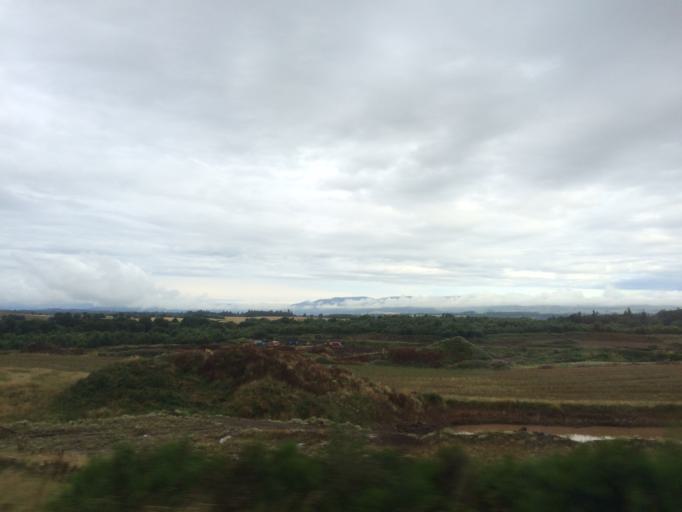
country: GB
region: Scotland
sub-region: Perth and Kinross
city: Auchterarder
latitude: 56.3007
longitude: -3.6635
